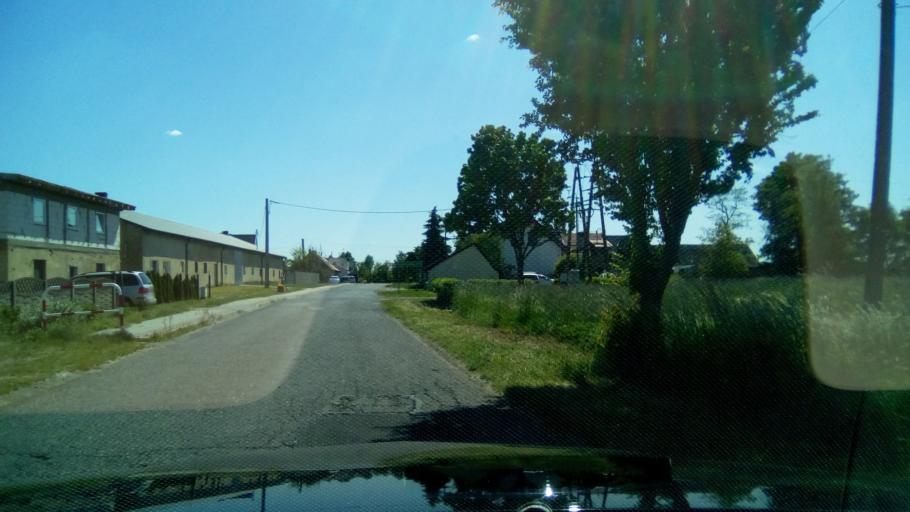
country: PL
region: Greater Poland Voivodeship
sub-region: Powiat gnieznienski
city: Gniezno
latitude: 52.4698
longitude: 17.5614
